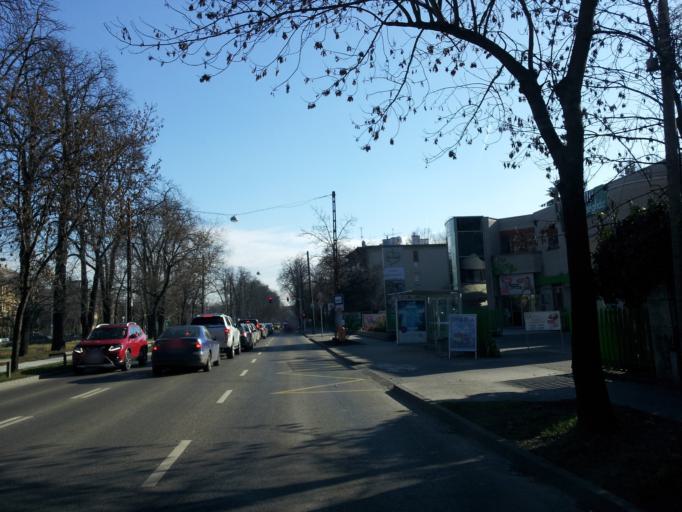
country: HU
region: Budapest
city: Budapest XII. keruelet
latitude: 47.5226
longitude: 18.9890
